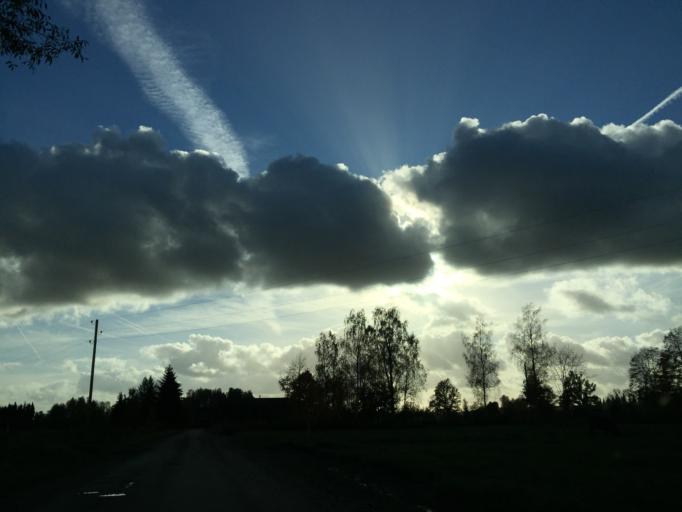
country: LV
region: Ogre
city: Jumprava
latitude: 56.7834
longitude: 24.9152
